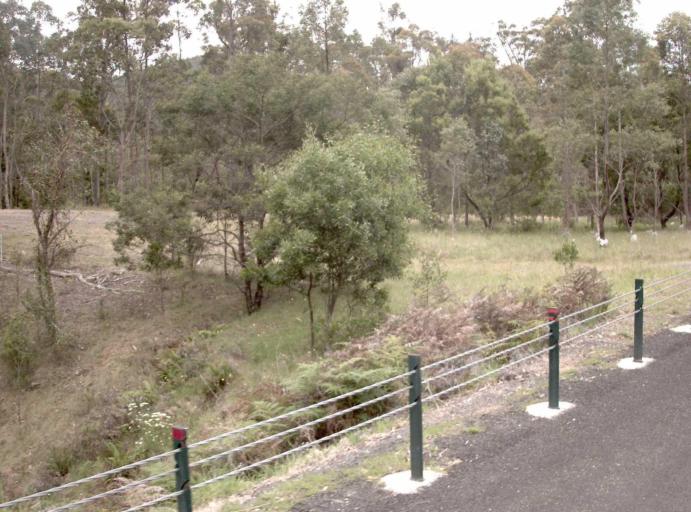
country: AU
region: New South Wales
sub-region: Bombala
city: Bombala
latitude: -37.2584
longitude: 149.2384
